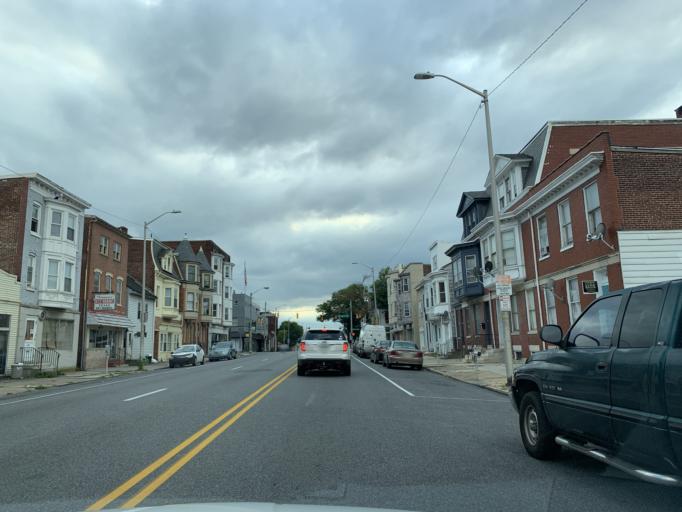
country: US
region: Pennsylvania
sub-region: York County
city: West York
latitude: 39.9574
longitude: -76.7443
